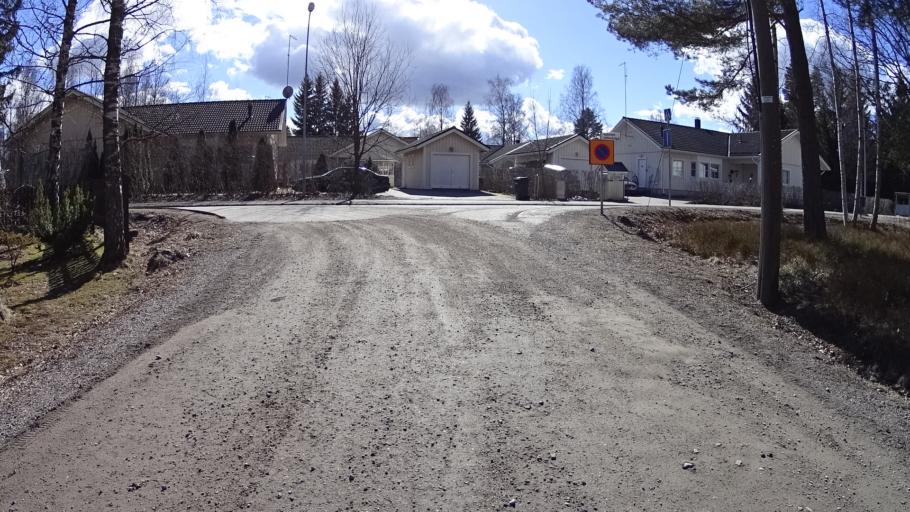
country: FI
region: Uusimaa
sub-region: Helsinki
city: Kauniainen
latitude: 60.2261
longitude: 24.7046
